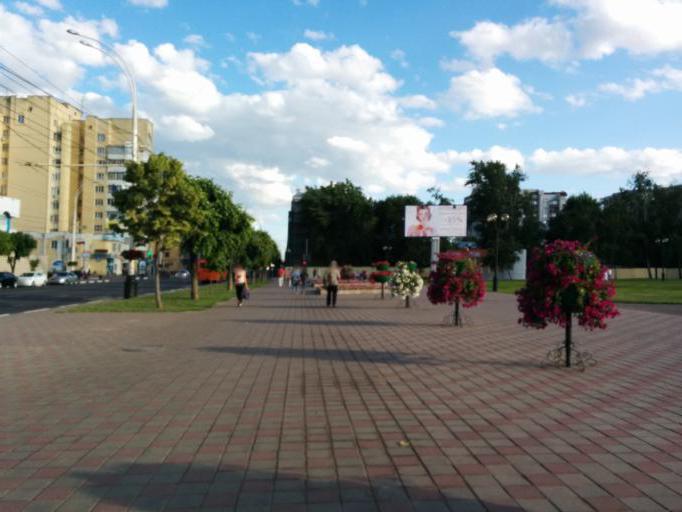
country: RU
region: Tambov
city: Tambov
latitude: 52.7332
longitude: 41.4530
